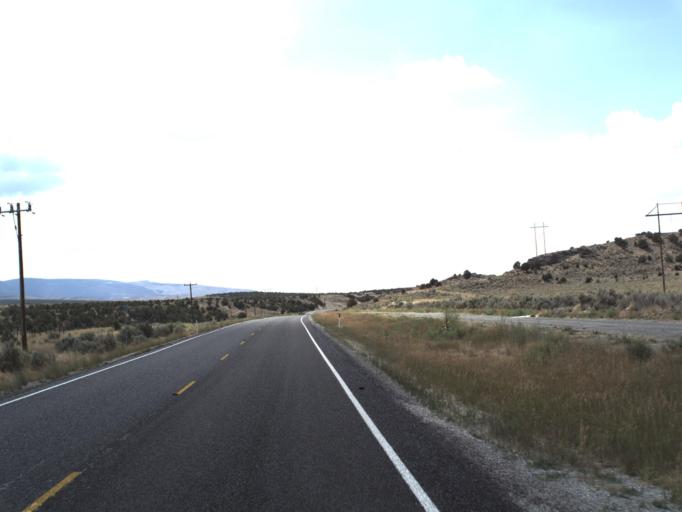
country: US
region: Idaho
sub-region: Minidoka County
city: Rupert
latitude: 41.9716
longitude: -113.1415
